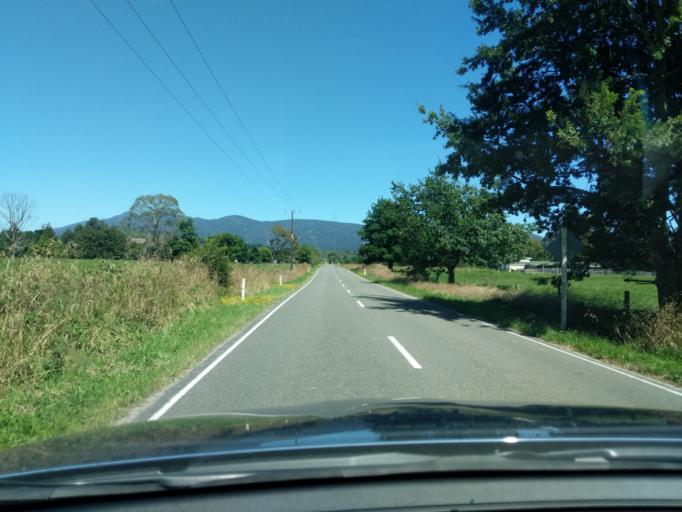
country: NZ
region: Tasman
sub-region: Tasman District
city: Takaka
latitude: -40.7290
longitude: 172.6344
